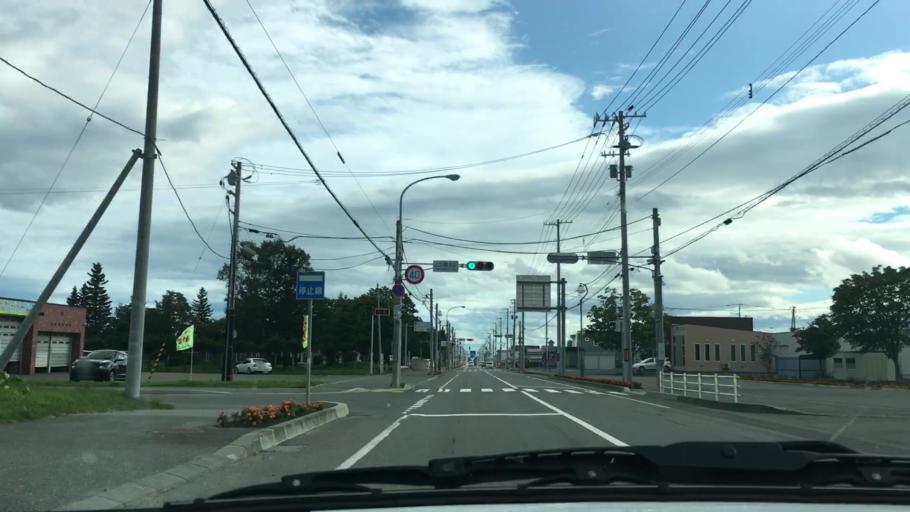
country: JP
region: Hokkaido
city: Otofuke
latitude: 43.2333
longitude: 143.2952
